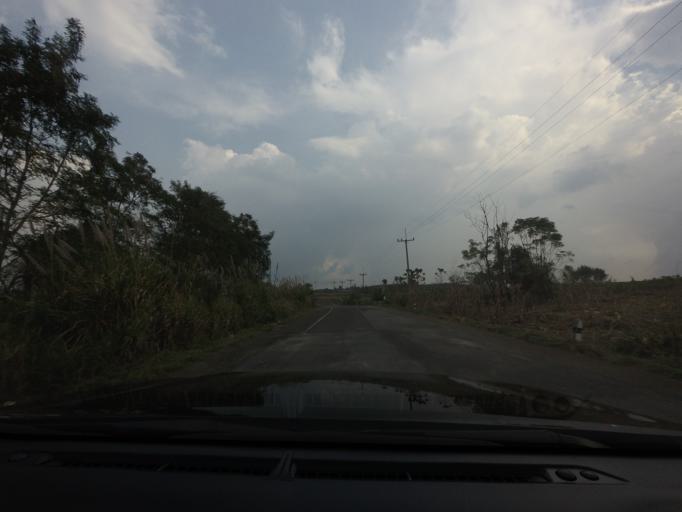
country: TH
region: Nakhon Ratchasima
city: Wang Nam Khiao
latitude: 14.4132
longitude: 101.7675
